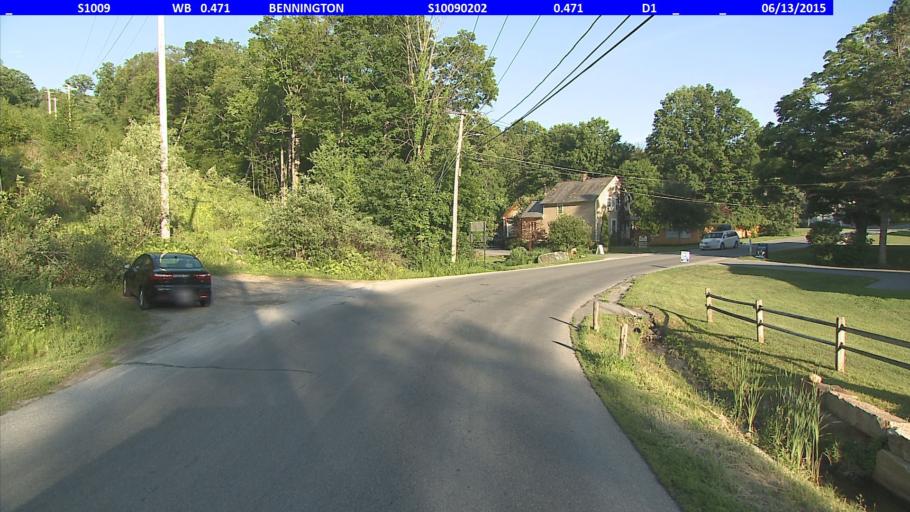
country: US
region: Vermont
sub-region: Bennington County
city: Bennington
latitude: 42.8899
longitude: -73.1809
